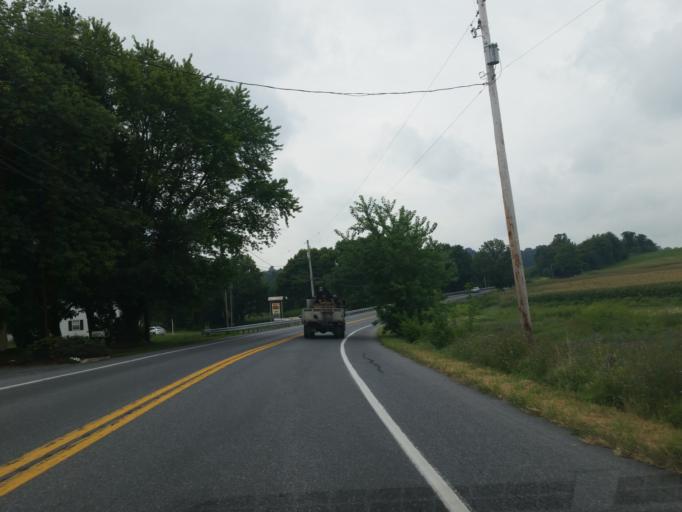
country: US
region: Pennsylvania
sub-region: Lancaster County
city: Brickerville
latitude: 40.2060
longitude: -76.2985
